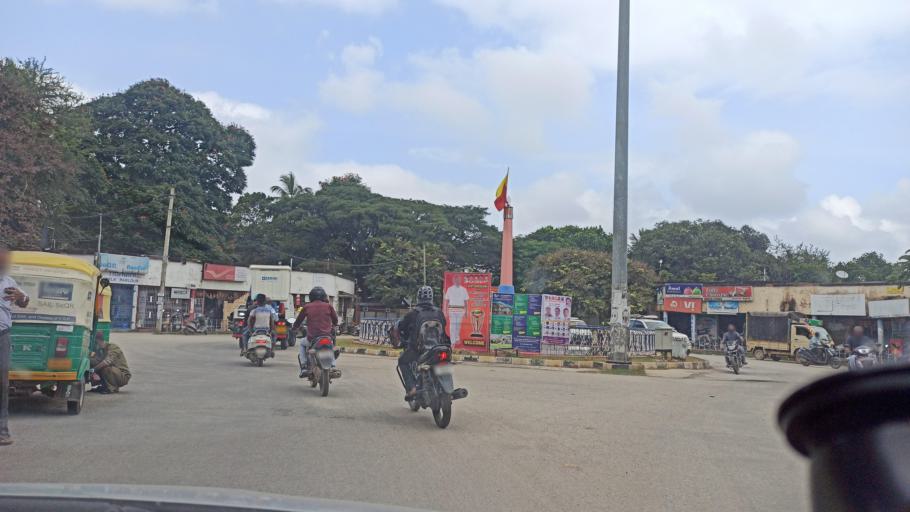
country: IN
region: Karnataka
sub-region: Bangalore Urban
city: Bangalore
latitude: 13.0075
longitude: 77.6835
